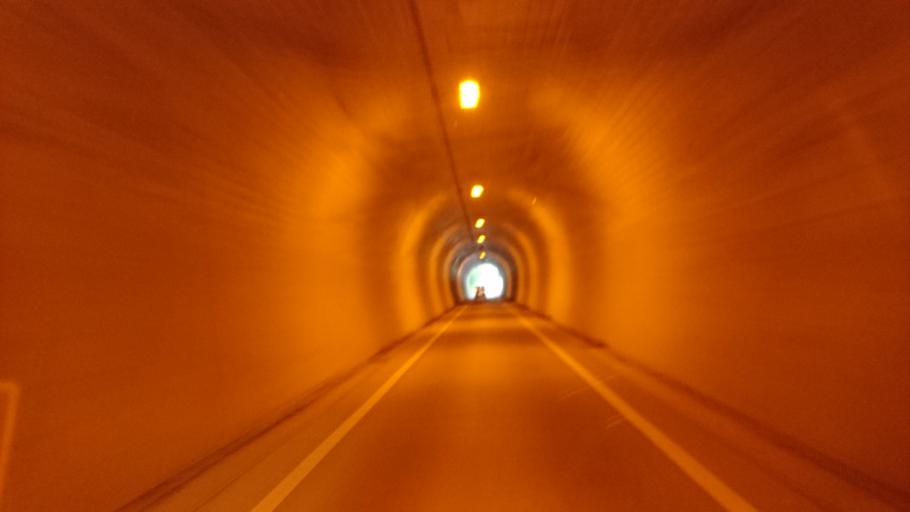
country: JP
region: Chiba
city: Kawaguchi
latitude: 35.1751
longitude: 140.0119
